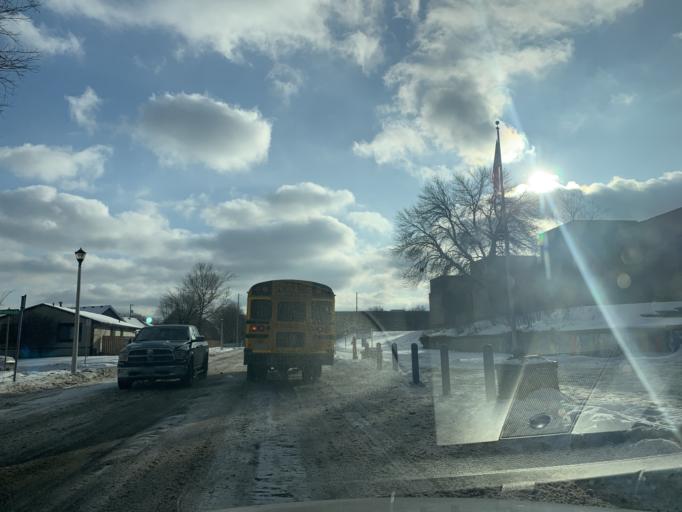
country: US
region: Minnesota
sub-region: Hennepin County
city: Minneapolis
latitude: 44.9944
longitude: -93.2896
